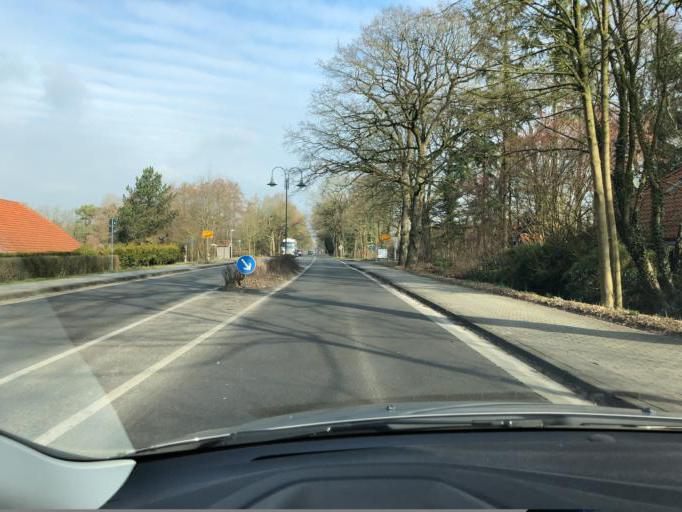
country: DE
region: Lower Saxony
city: Hesel
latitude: 53.3096
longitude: 7.5950
